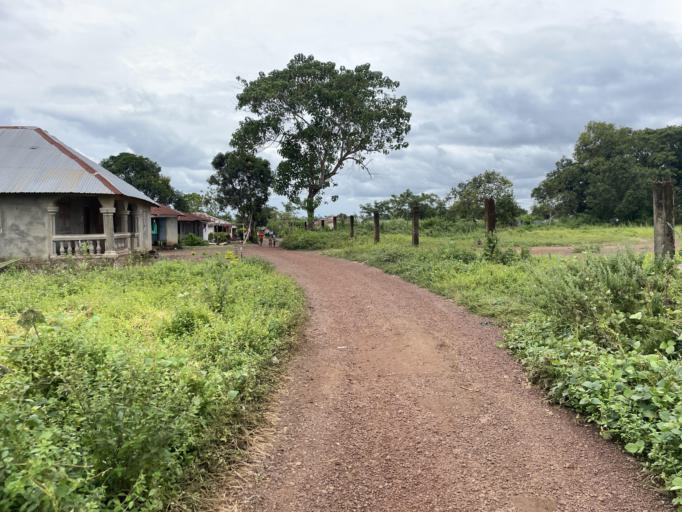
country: SL
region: Northern Province
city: Kambia
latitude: 9.1302
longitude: -12.9080
